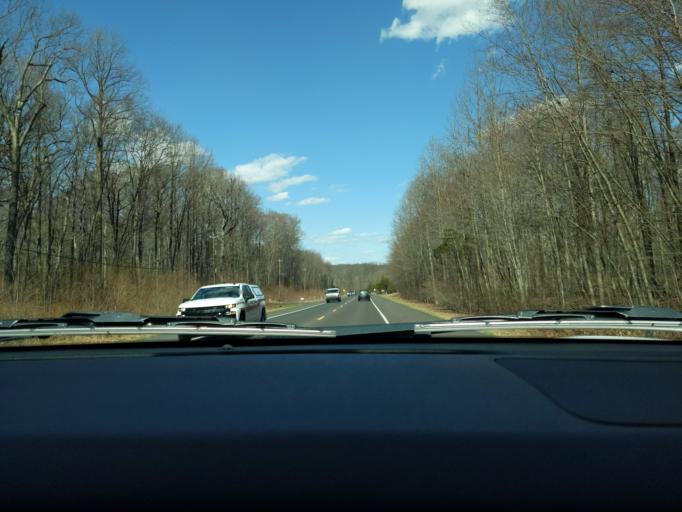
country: US
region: Pennsylvania
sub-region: Bucks County
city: Perkasie
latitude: 40.4287
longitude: -75.2702
